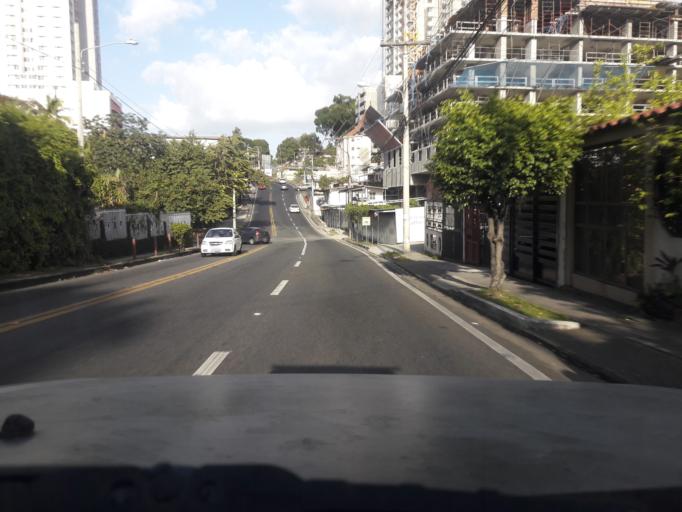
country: PA
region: Panama
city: Panama
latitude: 9.0136
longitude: -79.5086
